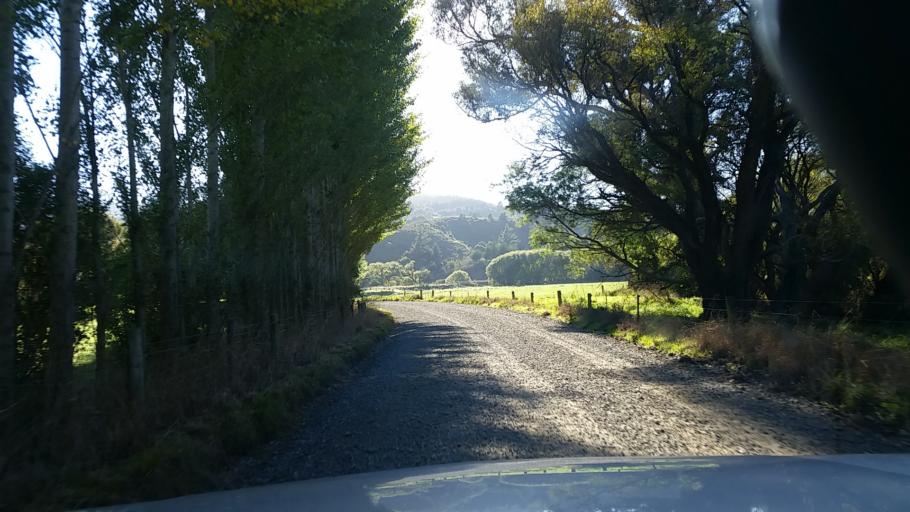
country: NZ
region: Marlborough
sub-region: Marlborough District
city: Blenheim
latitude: -41.4427
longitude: 173.8974
